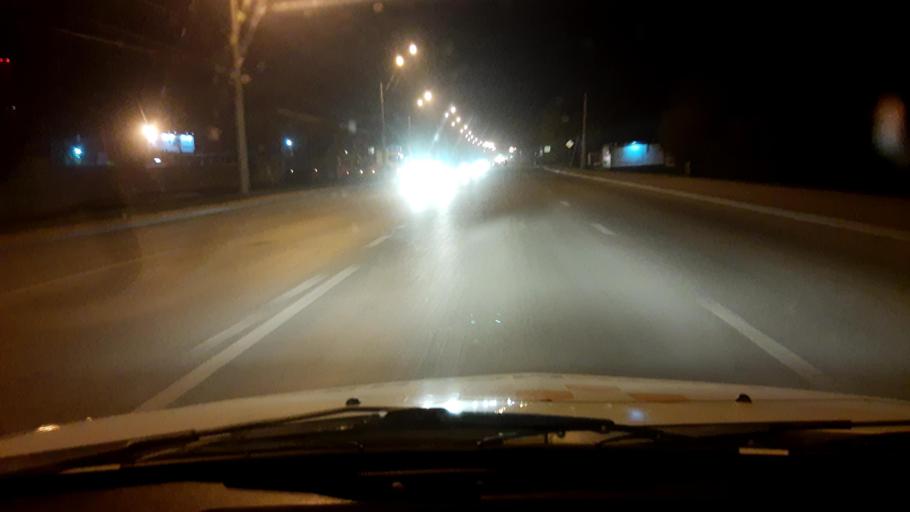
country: RU
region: Bashkortostan
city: Iglino
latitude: 54.7659
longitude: 56.2364
